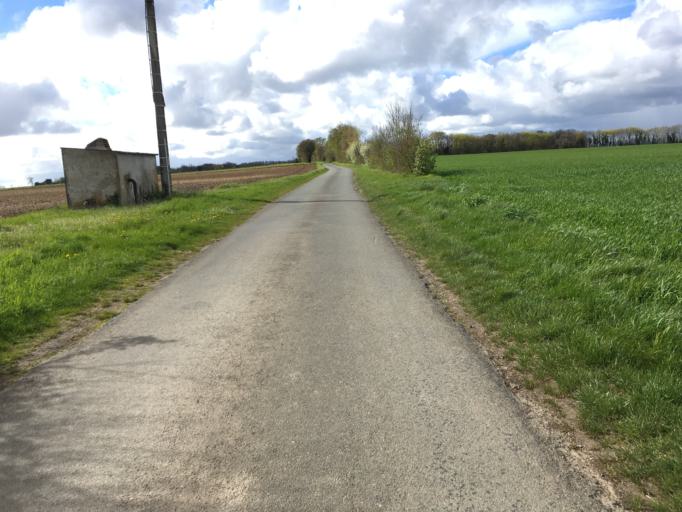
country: FR
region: Poitou-Charentes
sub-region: Departement de la Charente-Maritime
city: Le Thou
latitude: 46.1286
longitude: -0.8612
